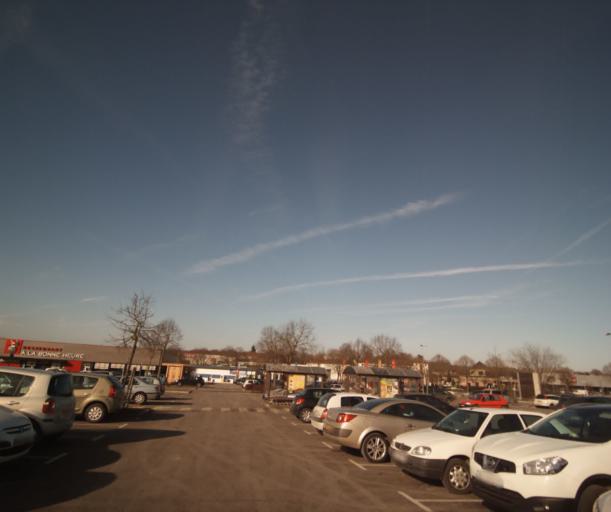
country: FR
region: Franche-Comte
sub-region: Departement du Doubs
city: Franois
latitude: 47.2164
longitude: 5.9484
